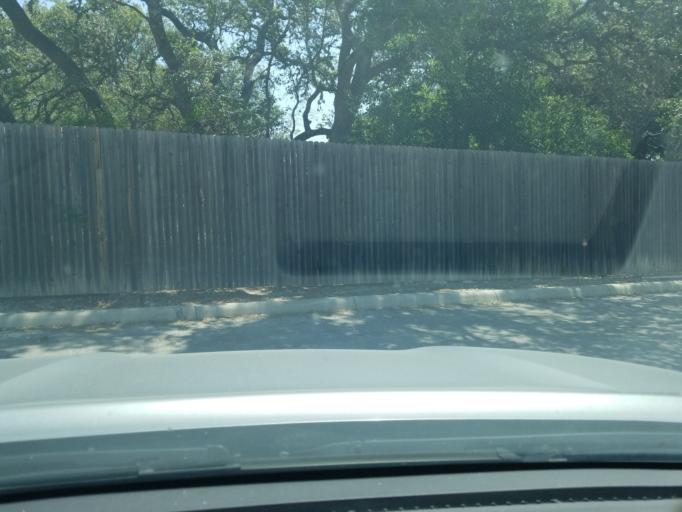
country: US
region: Texas
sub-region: Bexar County
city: Timberwood Park
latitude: 29.7060
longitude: -98.4811
